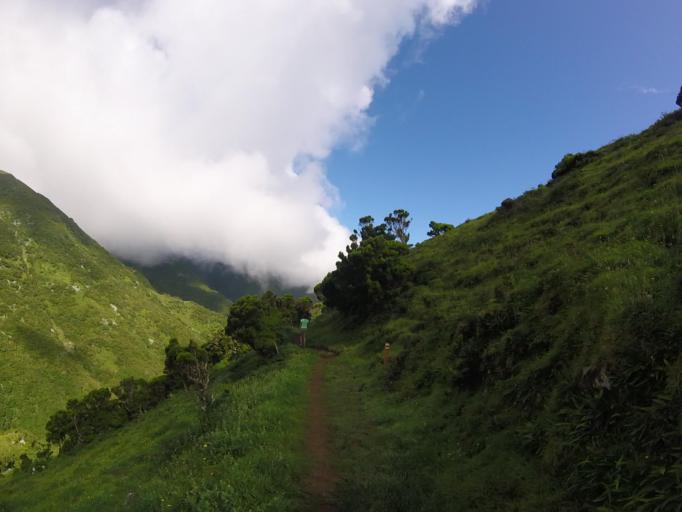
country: PT
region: Azores
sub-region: Sao Roque do Pico
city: Sao Roque do Pico
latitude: 38.6027
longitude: -27.9208
